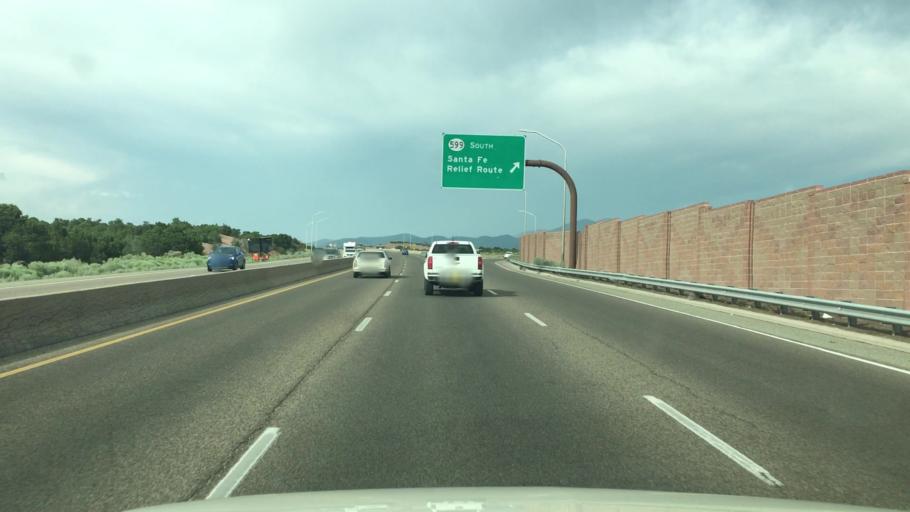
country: US
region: New Mexico
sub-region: Santa Fe County
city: Santa Fe
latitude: 35.7064
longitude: -105.9434
